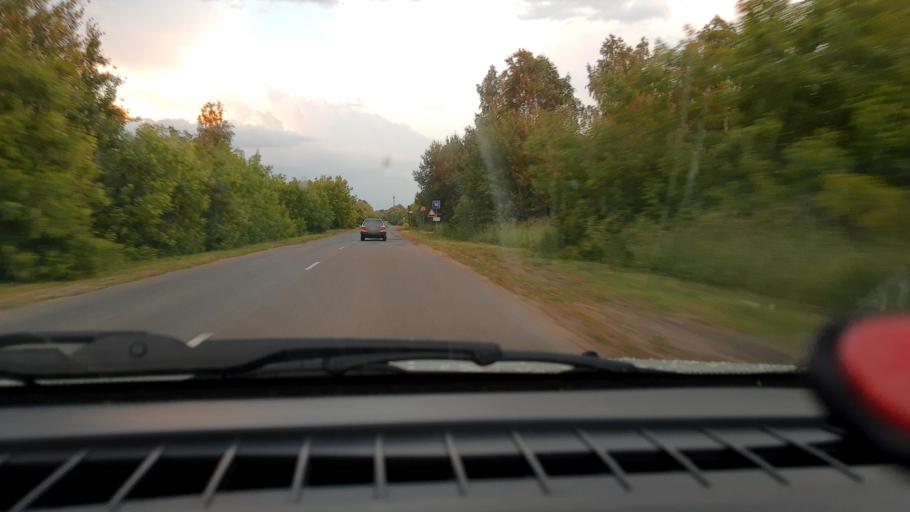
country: RU
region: Nizjnij Novgorod
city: Kstovo
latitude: 56.1315
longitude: 44.0660
